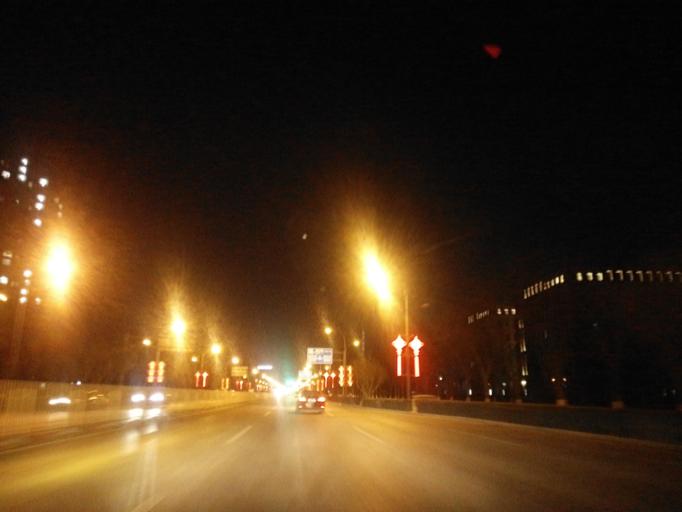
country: CN
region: Beijing
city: Jiugong
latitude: 39.7603
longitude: 116.5061
